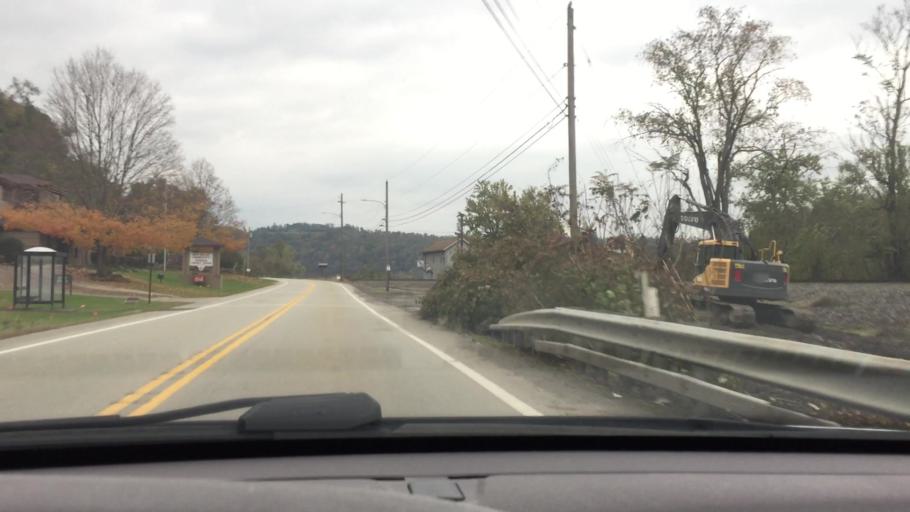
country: US
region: Pennsylvania
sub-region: Fayette County
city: Fairhope
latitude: 40.1013
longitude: -79.8458
